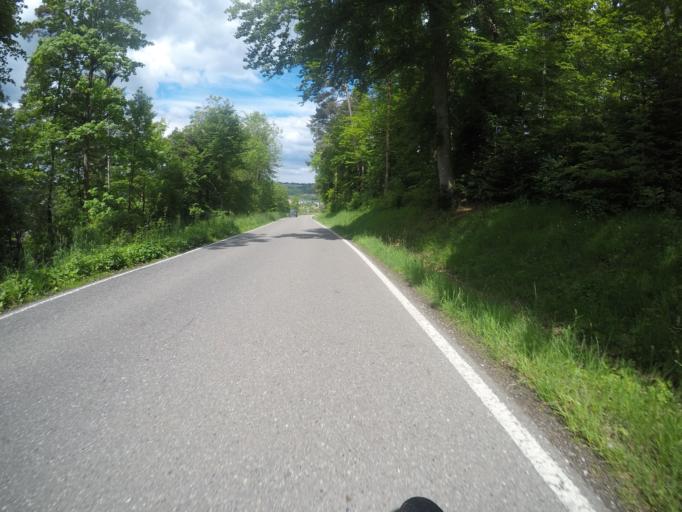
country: DE
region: Baden-Wuerttemberg
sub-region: Regierungsbezirk Stuttgart
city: Oberjettingen
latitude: 48.5815
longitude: 8.7410
